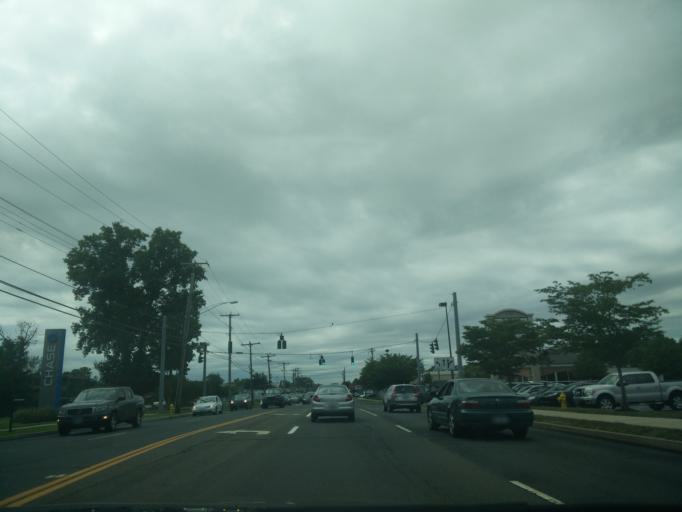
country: US
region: Connecticut
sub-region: New Haven County
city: Orange
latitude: 41.2477
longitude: -73.0251
